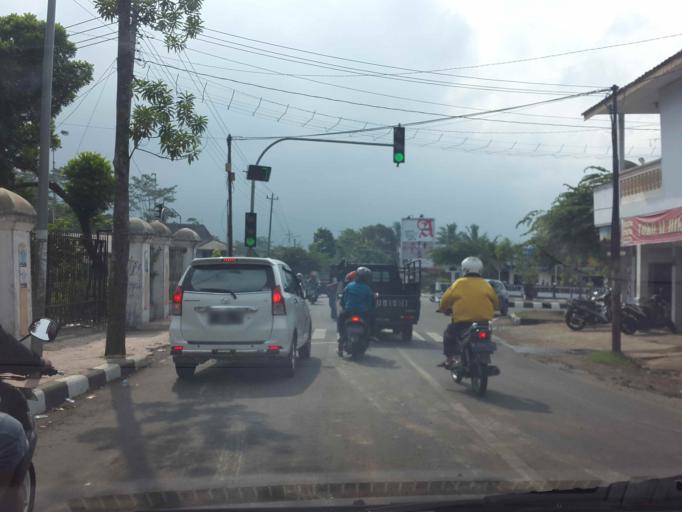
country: ID
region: Central Java
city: Salatiga
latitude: -7.3199
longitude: 110.4792
